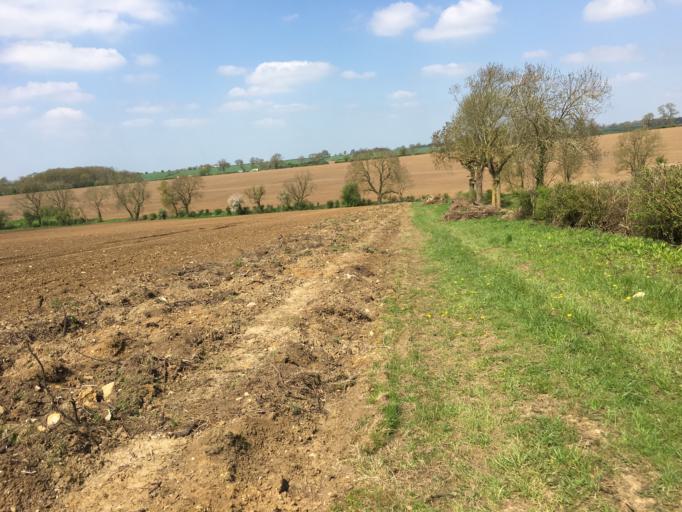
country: GB
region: England
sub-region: Leicestershire
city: Houghton on the Hill
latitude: 52.6050
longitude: -0.9921
